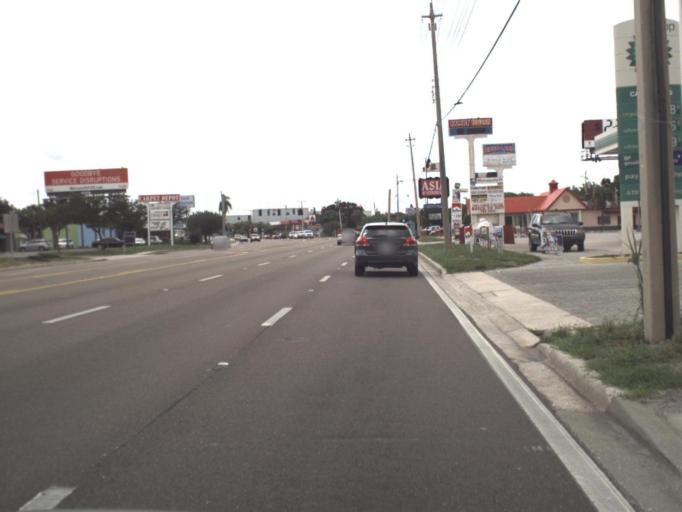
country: US
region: Florida
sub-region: Manatee County
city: Whitfield
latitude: 27.4202
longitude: -82.5756
